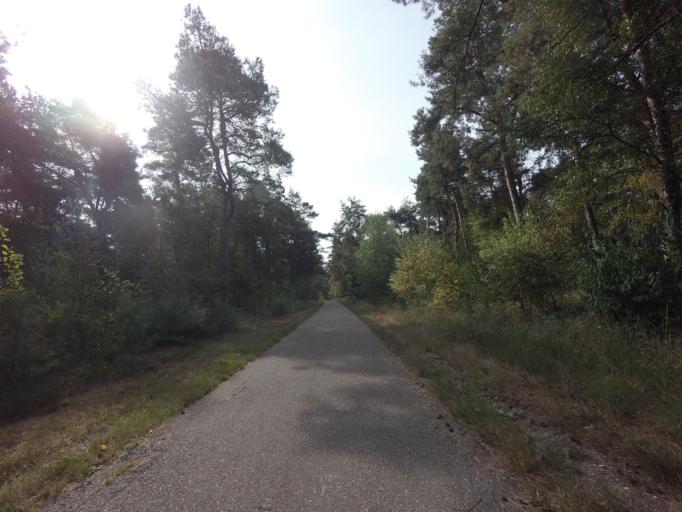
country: NL
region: North Brabant
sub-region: Gemeente Mill en Sint Hubert
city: Wilbertoord
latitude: 51.6148
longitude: 5.8163
